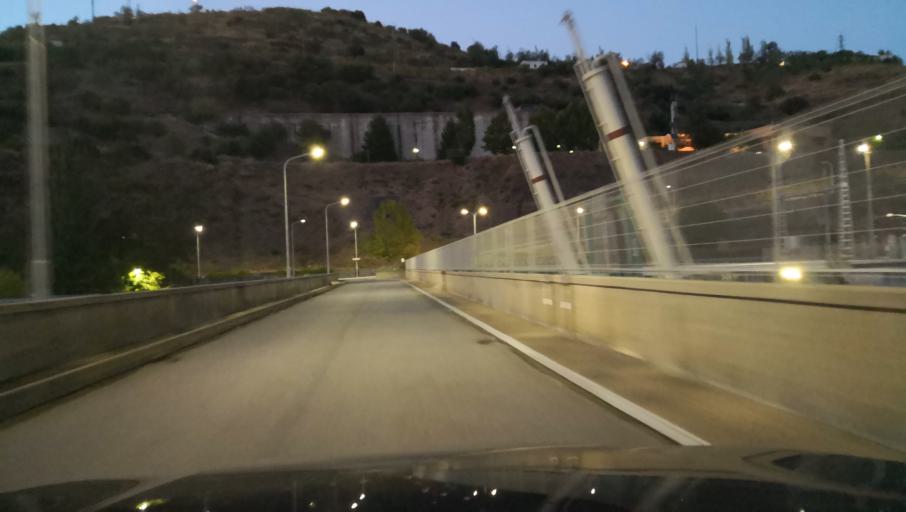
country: PT
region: Vila Real
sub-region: Peso da Regua
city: Peso da Regua
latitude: 41.1471
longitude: -7.7396
